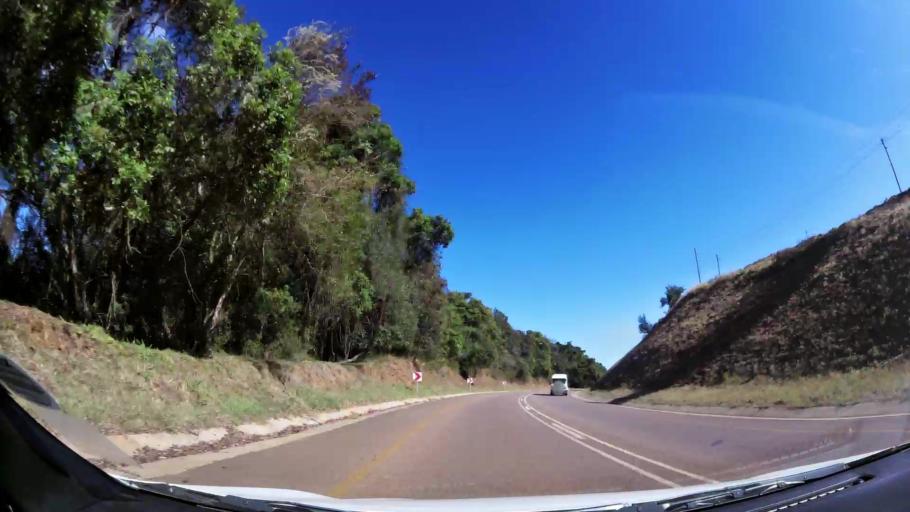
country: ZA
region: Limpopo
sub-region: Capricorn District Municipality
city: Mankoeng
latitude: -23.9175
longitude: 29.9599
